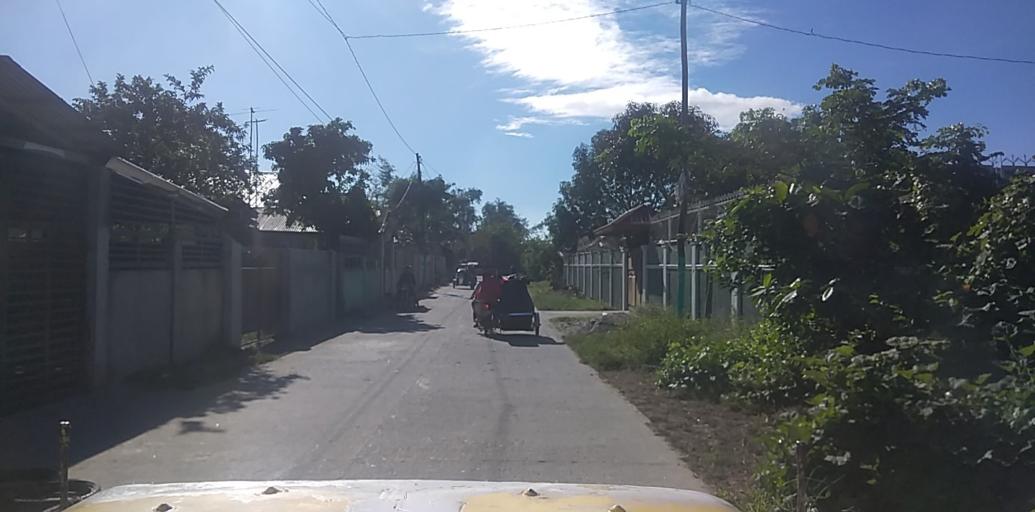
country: PH
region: Central Luzon
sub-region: Province of Pampanga
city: San Patricio
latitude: 15.1132
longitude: 120.7105
